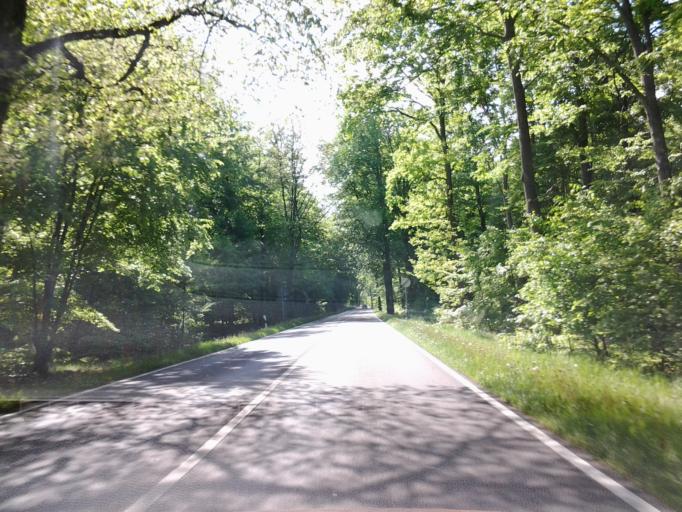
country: DE
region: Brandenburg
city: Oranienburg
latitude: 52.7645
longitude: 13.3060
